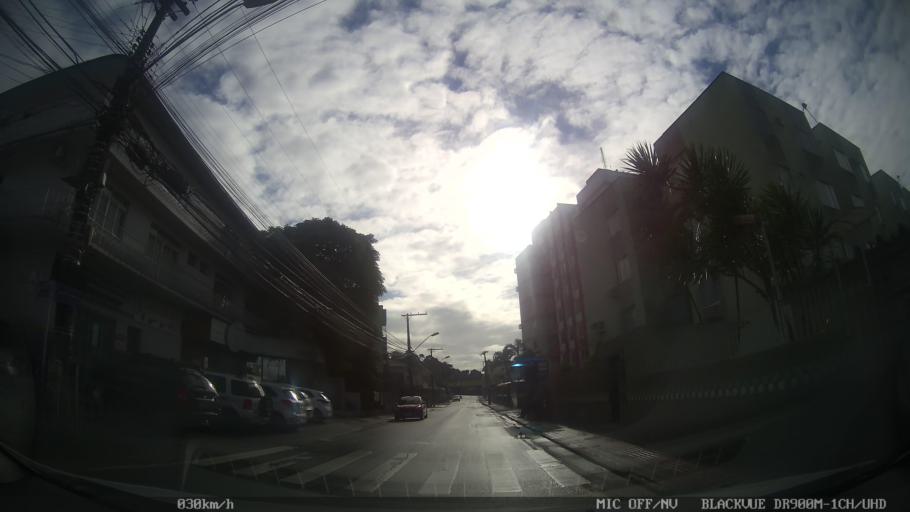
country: BR
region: Santa Catarina
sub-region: Sao Jose
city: Campinas
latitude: -27.6041
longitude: -48.6273
